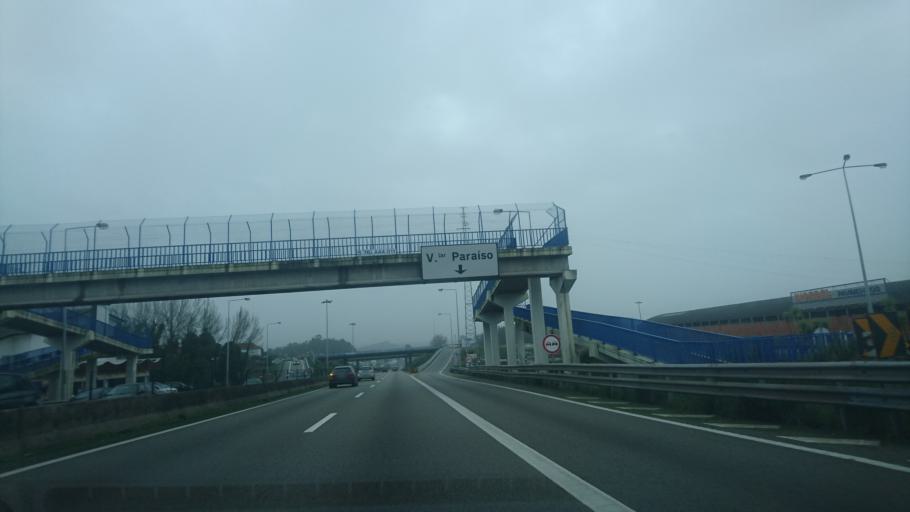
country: PT
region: Porto
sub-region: Vila Nova de Gaia
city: Vilar do Paraiso
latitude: 41.1100
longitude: -8.6260
